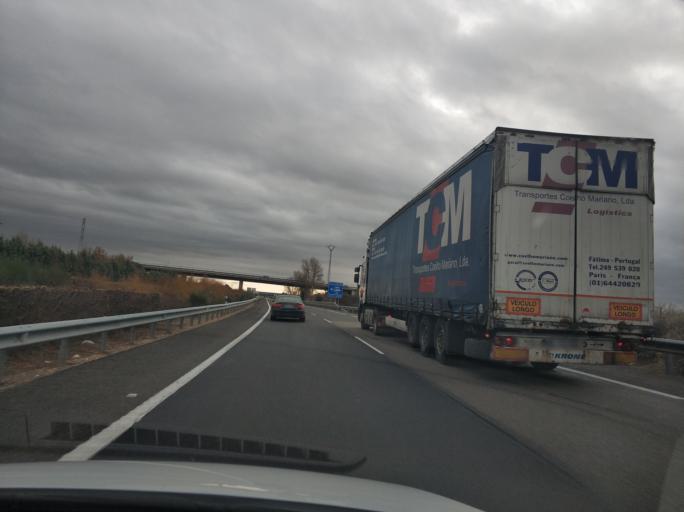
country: ES
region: Castille and Leon
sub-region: Provincia de Valladolid
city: Tordesillas
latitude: 41.5052
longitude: -5.0212
